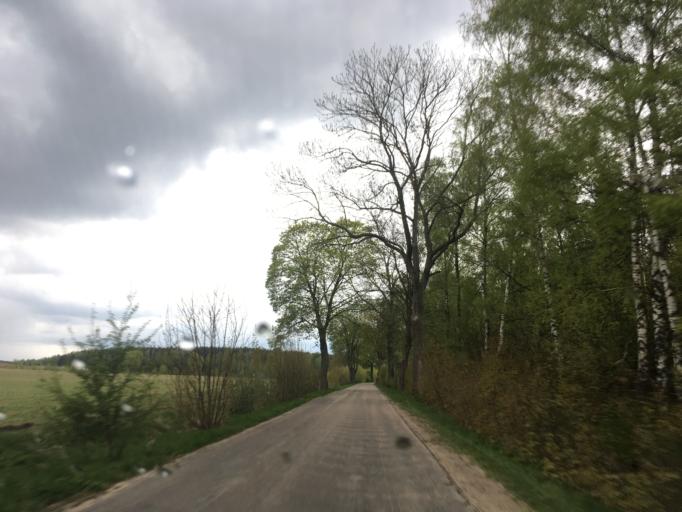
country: PL
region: Warmian-Masurian Voivodeship
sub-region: Powiat nidzicki
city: Kozlowo
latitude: 53.4170
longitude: 20.2148
